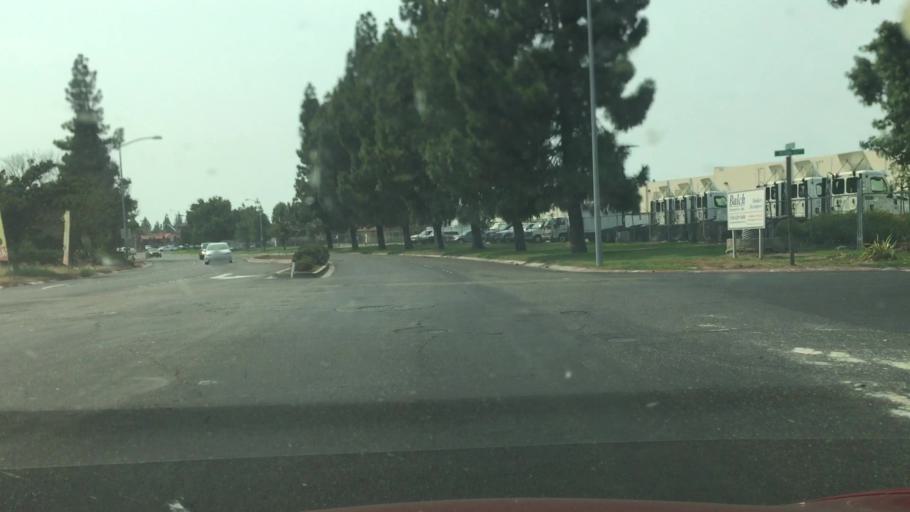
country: US
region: California
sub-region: San Joaquin County
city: Manteca
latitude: 37.7876
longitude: -121.2133
